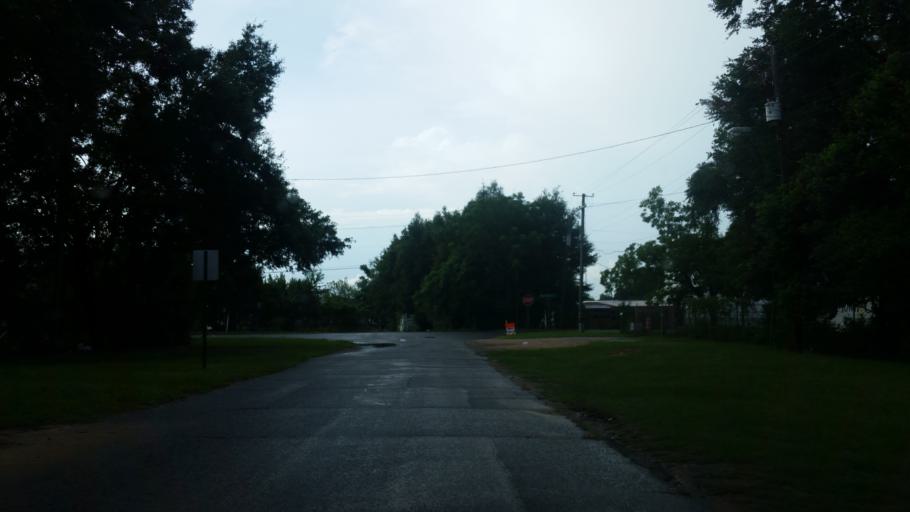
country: US
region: Florida
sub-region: Escambia County
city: Brent
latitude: 30.4586
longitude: -87.2411
